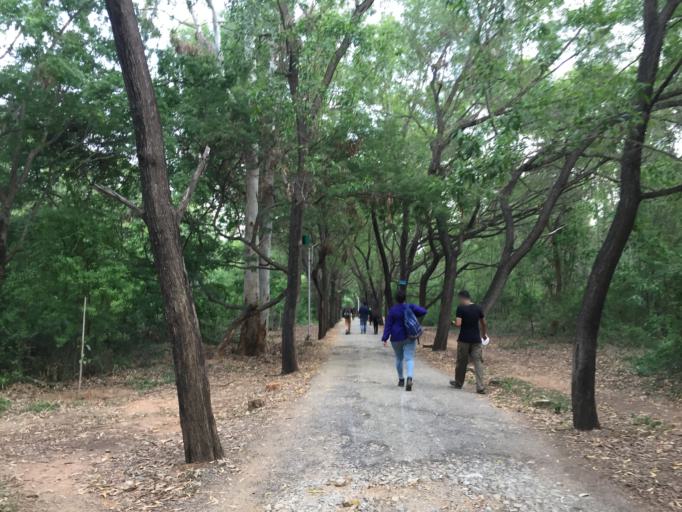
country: IN
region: Karnataka
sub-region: Bangalore Urban
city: Bangalore
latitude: 12.8945
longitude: 77.5924
